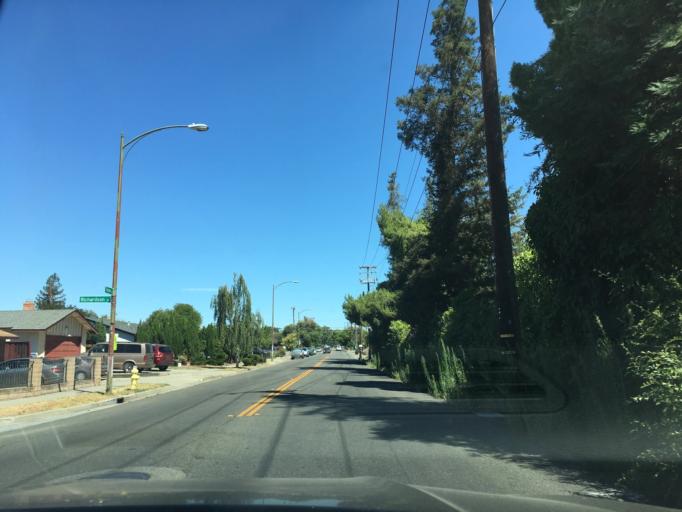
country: US
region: California
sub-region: Santa Clara County
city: East Foothills
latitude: 37.3859
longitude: -121.8296
